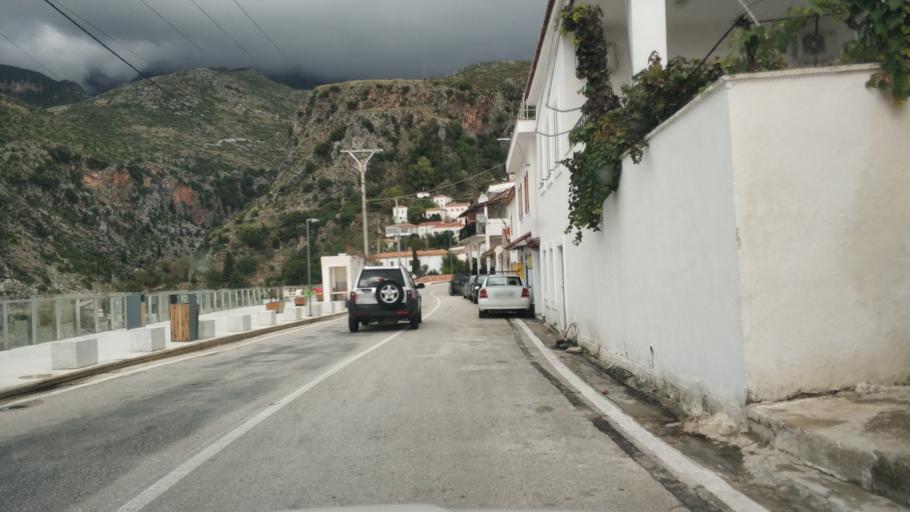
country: AL
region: Vlore
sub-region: Rrethi i Vlores
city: Vranisht
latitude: 40.1522
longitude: 19.6385
